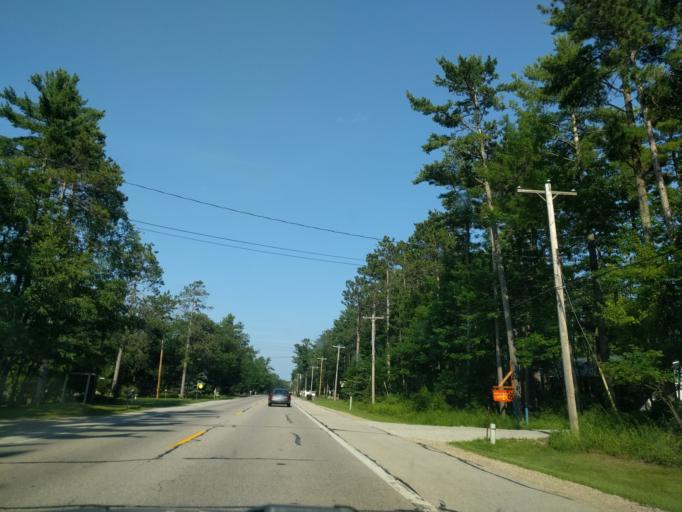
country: US
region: Michigan
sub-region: Delta County
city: Escanaba
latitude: 45.6819
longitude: -87.1330
